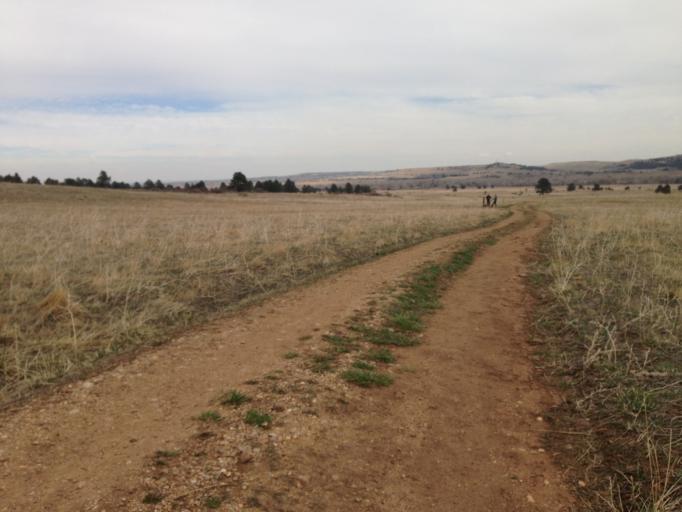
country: US
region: Colorado
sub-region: Boulder County
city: Boulder
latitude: 39.9548
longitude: -105.2615
